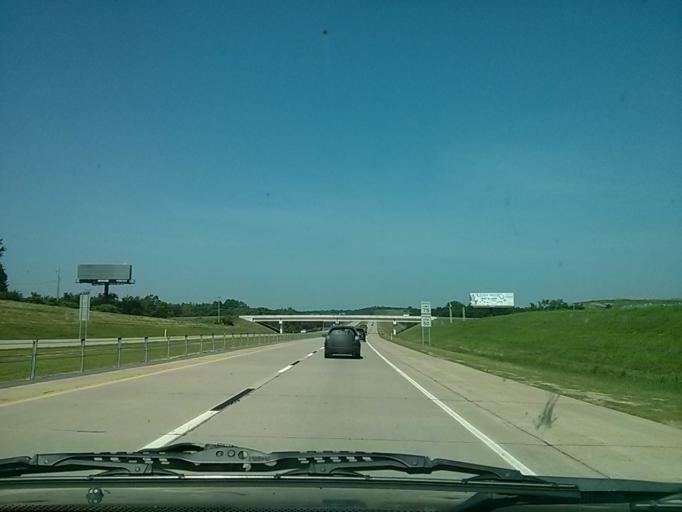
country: US
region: Oklahoma
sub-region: Tulsa County
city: Glenpool
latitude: 36.0092
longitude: -96.0239
